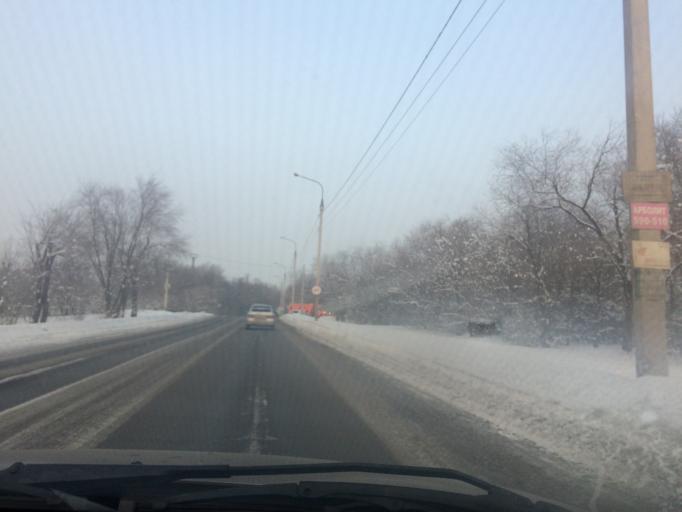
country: RU
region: Chelyabinsk
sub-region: Gorod Magnitogorsk
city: Magnitogorsk
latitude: 53.4632
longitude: 59.0676
